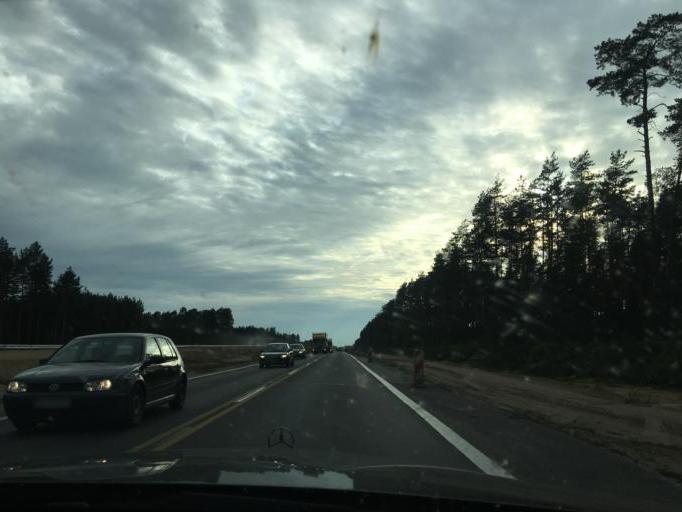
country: PL
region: Masovian Voivodeship
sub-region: Powiat ostrowski
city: Ostrow Mazowiecka
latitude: 52.7706
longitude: 21.8267
